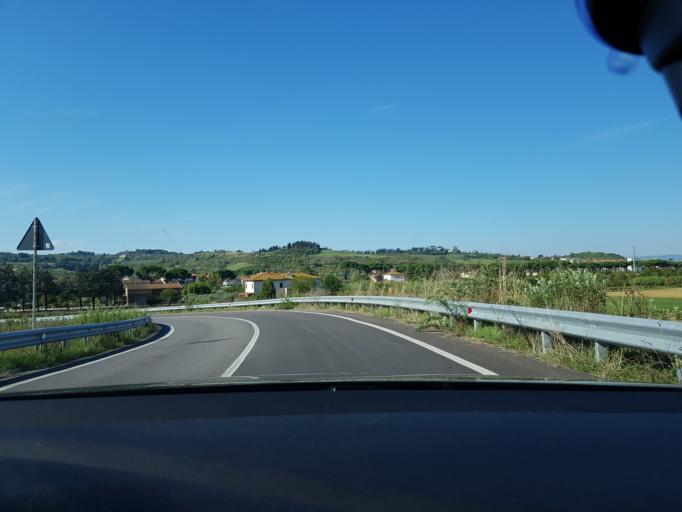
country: IT
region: Tuscany
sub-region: Province of Pisa
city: Ponte A Elsa
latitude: 43.6873
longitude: 10.9118
